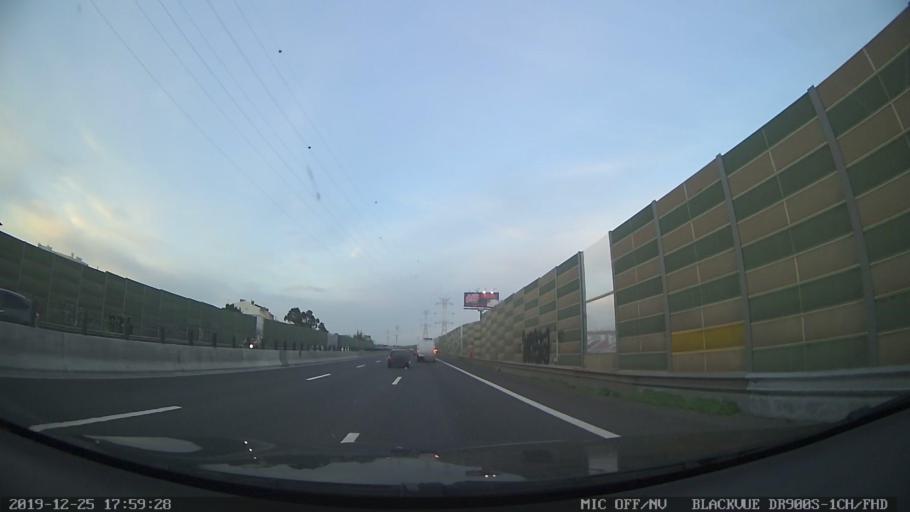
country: PT
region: Lisbon
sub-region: Loures
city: Bobadela
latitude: 38.8089
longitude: -9.1038
